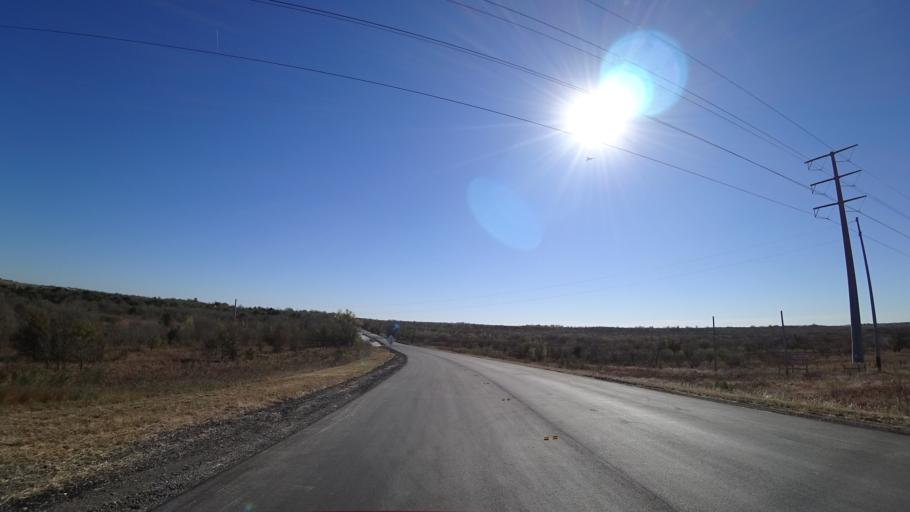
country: US
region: Texas
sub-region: Travis County
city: Garfield
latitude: 30.1169
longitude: -97.6590
